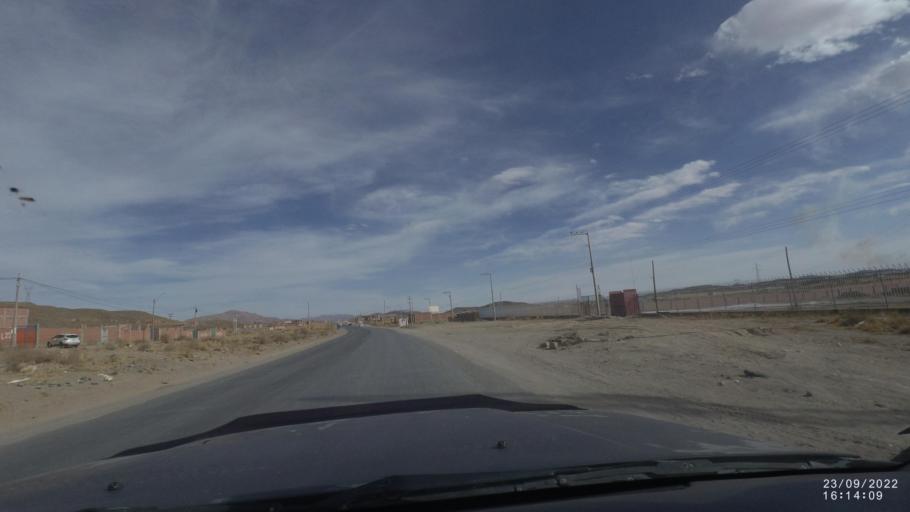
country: BO
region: Oruro
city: Oruro
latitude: -17.9883
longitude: -67.0489
